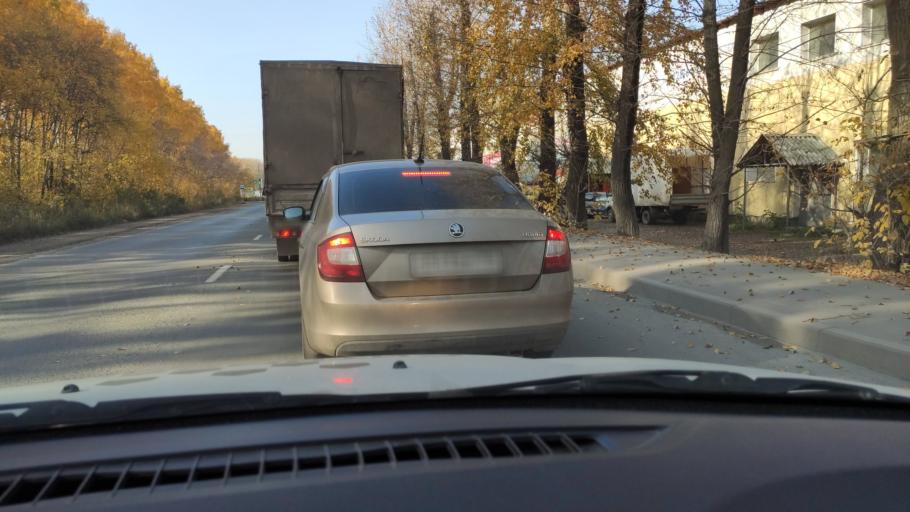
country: RU
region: Perm
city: Perm
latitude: 57.9565
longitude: 56.2166
